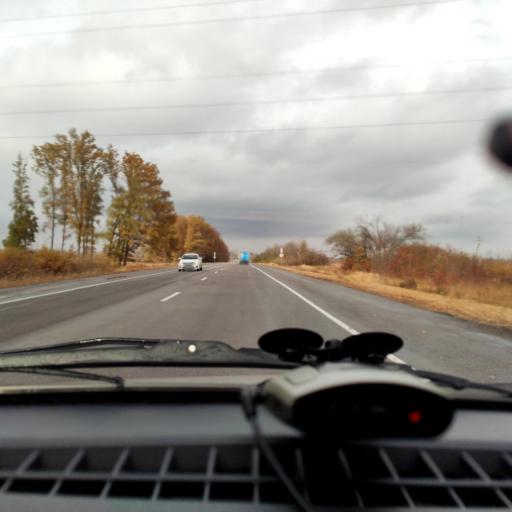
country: RU
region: Voronezj
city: Kolodeznyy
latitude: 51.3272
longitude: 39.0272
